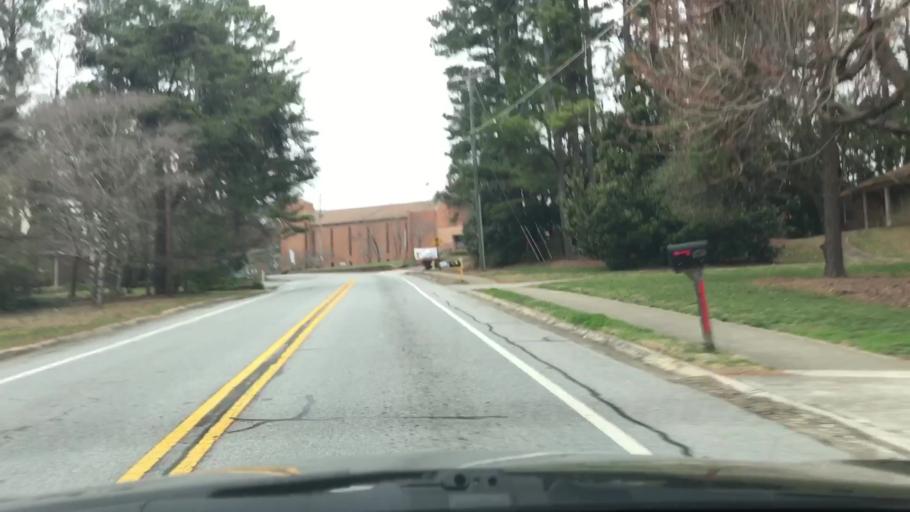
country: US
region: Georgia
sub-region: DeKalb County
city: Doraville
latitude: 33.9350
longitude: -84.2866
